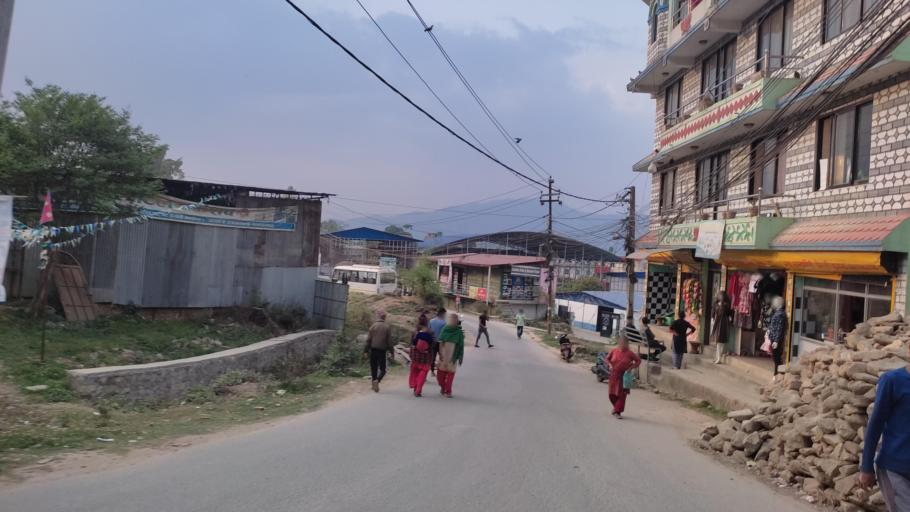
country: NP
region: Central Region
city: Kirtipur
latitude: 27.6709
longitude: 85.2484
